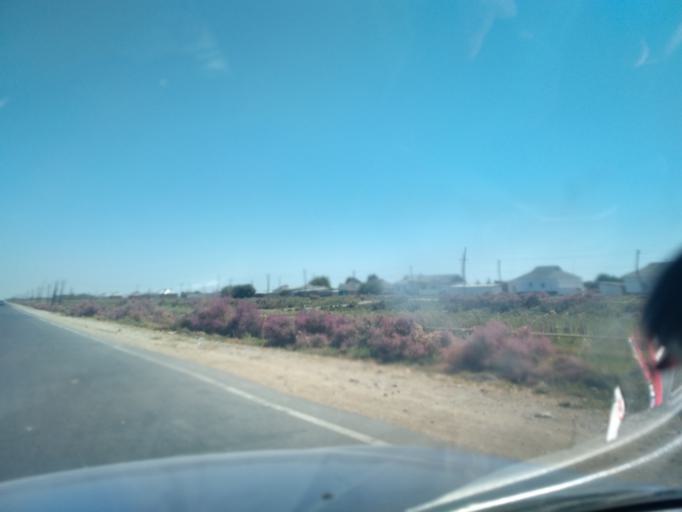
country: UZ
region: Sirdaryo
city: Guliston
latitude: 40.4910
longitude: 68.7077
